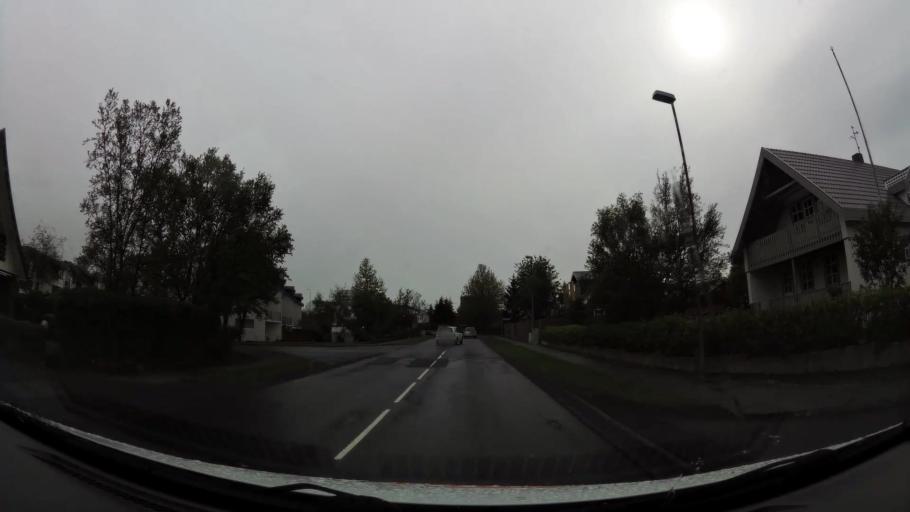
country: IS
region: Capital Region
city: Gardabaer
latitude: 64.0927
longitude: -21.9167
